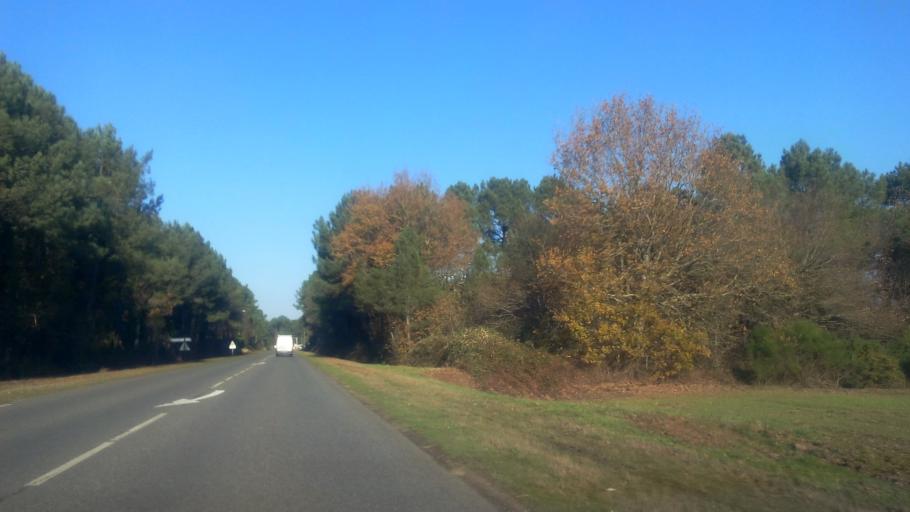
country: FR
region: Brittany
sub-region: Departement du Morbihan
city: Saint-Vincent-sur-Oust
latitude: 47.6852
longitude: -2.1386
